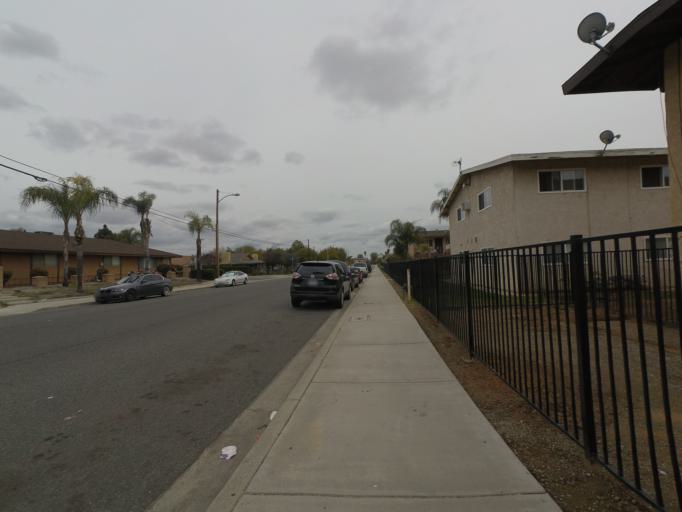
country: US
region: California
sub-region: Riverside County
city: March Air Force Base
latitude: 33.9183
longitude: -117.2685
